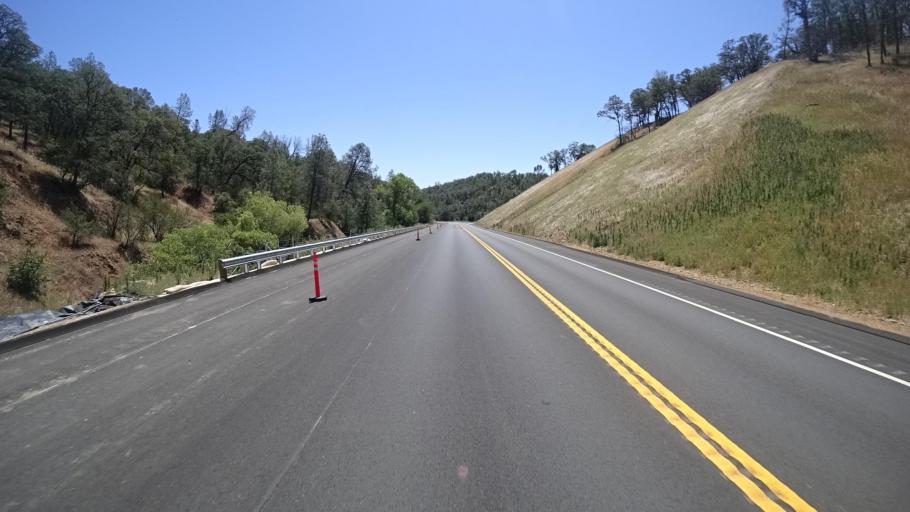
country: US
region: California
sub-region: Lake County
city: Hidden Valley Lake
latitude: 38.8360
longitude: -122.5893
